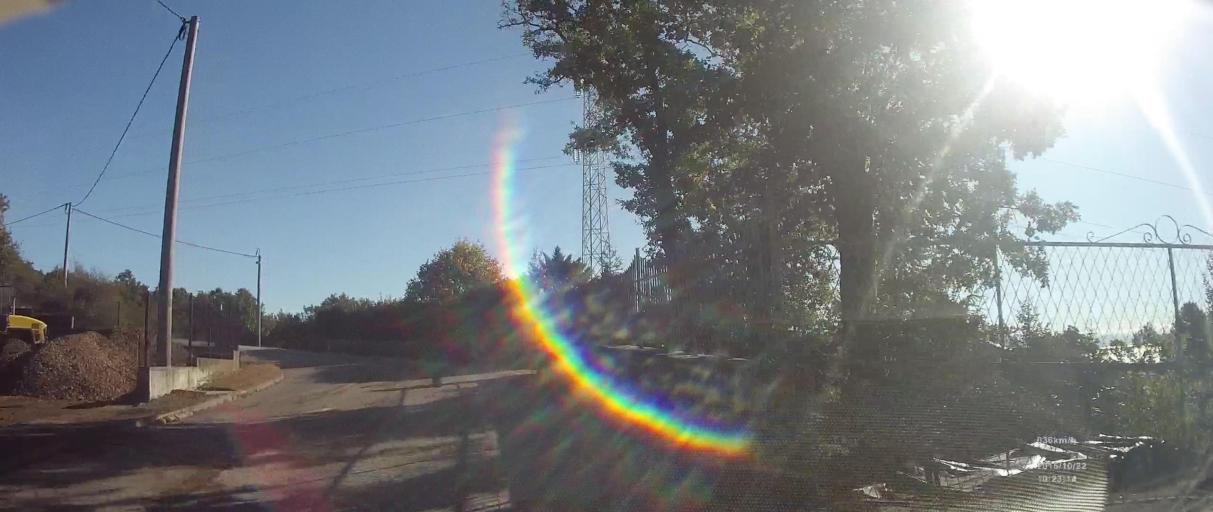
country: HR
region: Primorsko-Goranska
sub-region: Grad Opatija
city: Opatija
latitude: 45.3276
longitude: 14.2753
